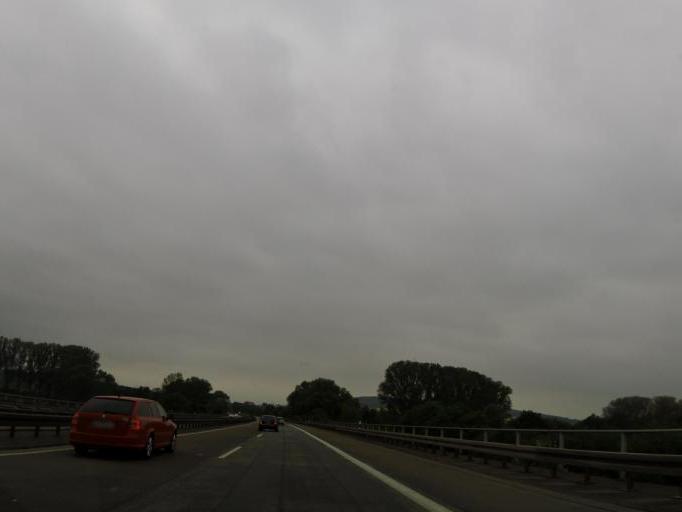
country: DE
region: Lower Saxony
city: Hillerse
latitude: 51.7276
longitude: 9.9566
